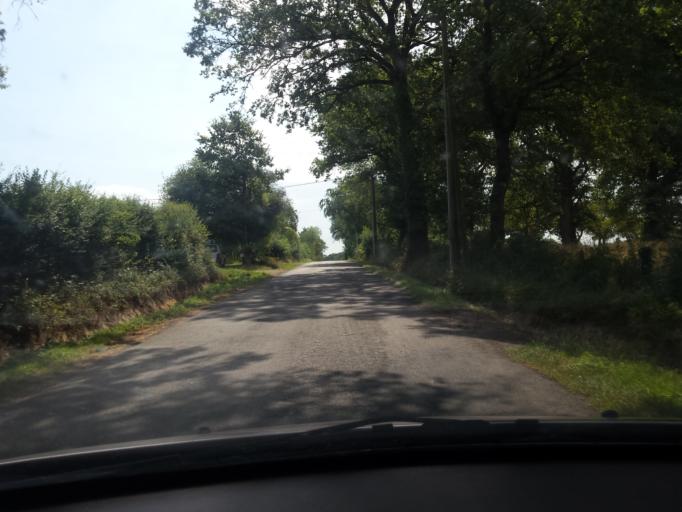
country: FR
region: Poitou-Charentes
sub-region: Departement de la Vienne
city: Availles-Limouzine
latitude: 46.0862
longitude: 0.7339
